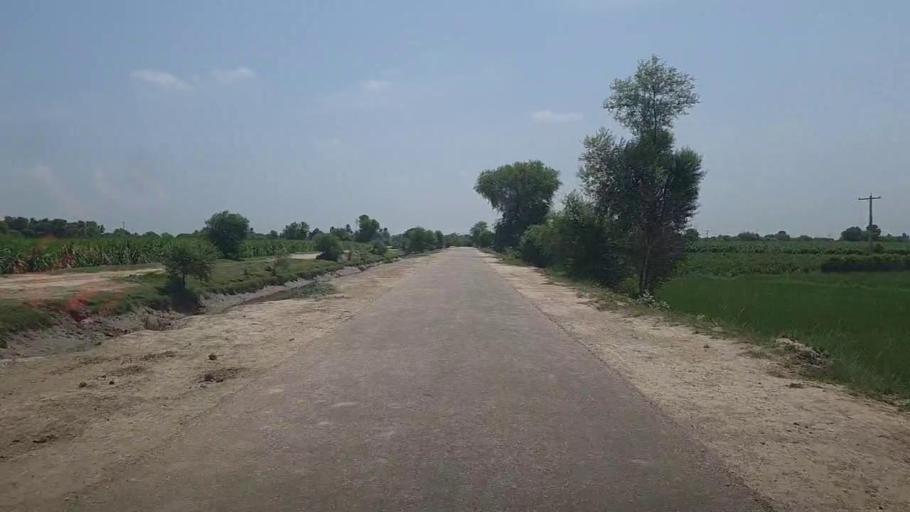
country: PK
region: Sindh
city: Ubauro
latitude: 28.2925
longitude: 69.8067
